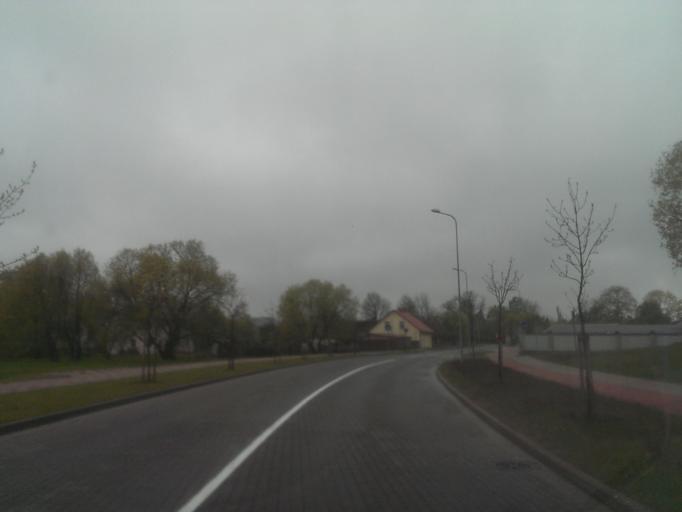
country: LV
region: Ventspils
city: Ventspils
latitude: 57.4048
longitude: 21.6014
